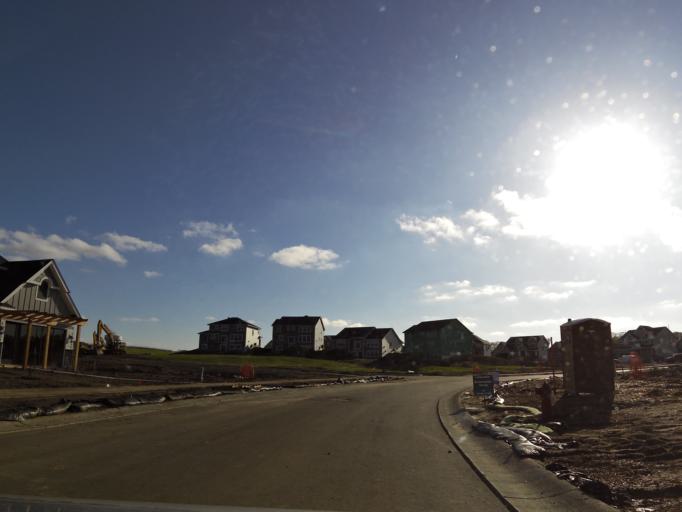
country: US
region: Minnesota
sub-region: Washington County
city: Lake Elmo
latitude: 44.9550
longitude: -92.9075
